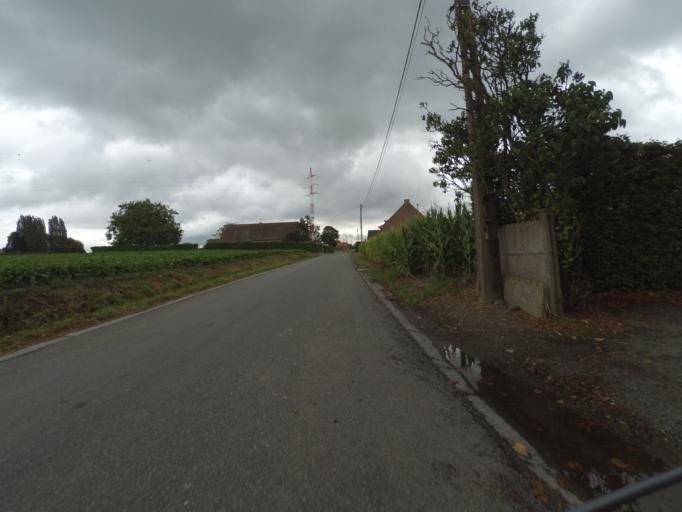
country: BE
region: Wallonia
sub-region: Province du Hainaut
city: Celles
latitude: 50.7364
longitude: 3.4693
